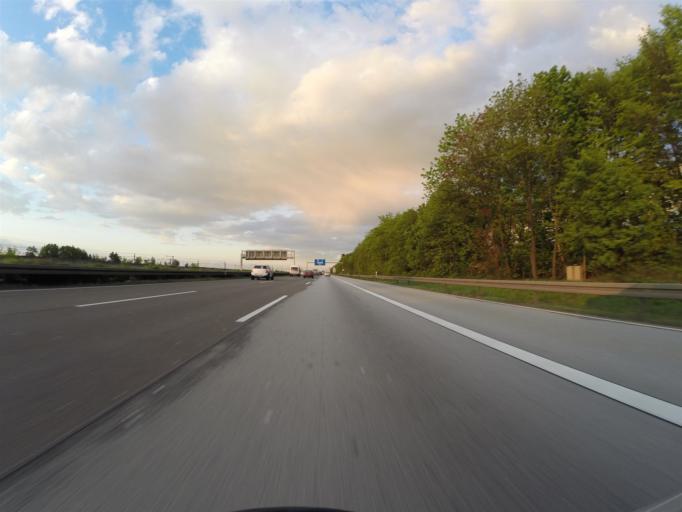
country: DE
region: Hesse
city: Kelsterbach
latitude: 50.0384
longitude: 8.5233
